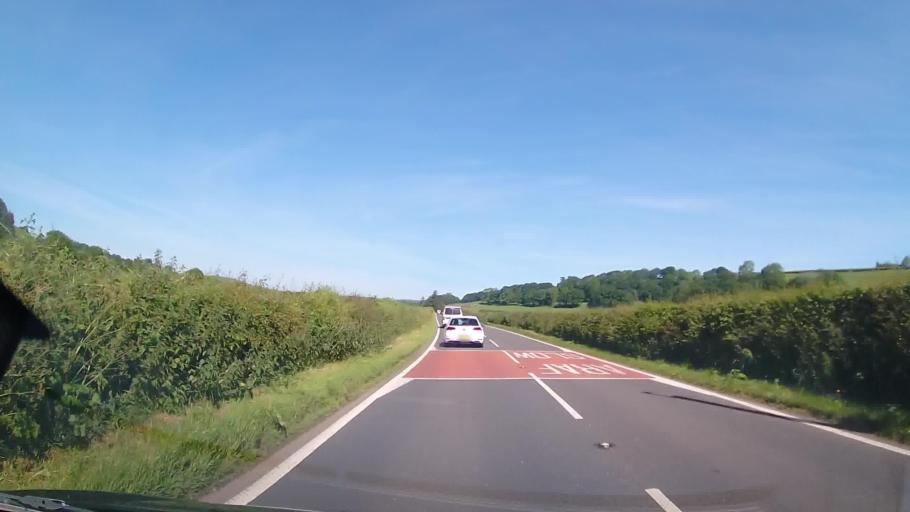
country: GB
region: Wales
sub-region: Sir Powys
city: Llangynog
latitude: 52.6780
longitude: -3.4358
